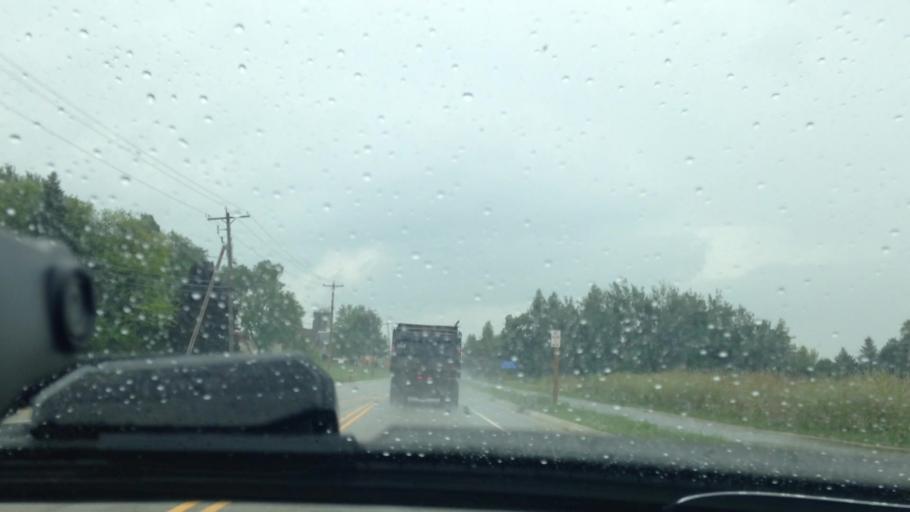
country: US
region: Wisconsin
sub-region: Washington County
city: Richfield
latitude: 43.2429
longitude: -88.1893
